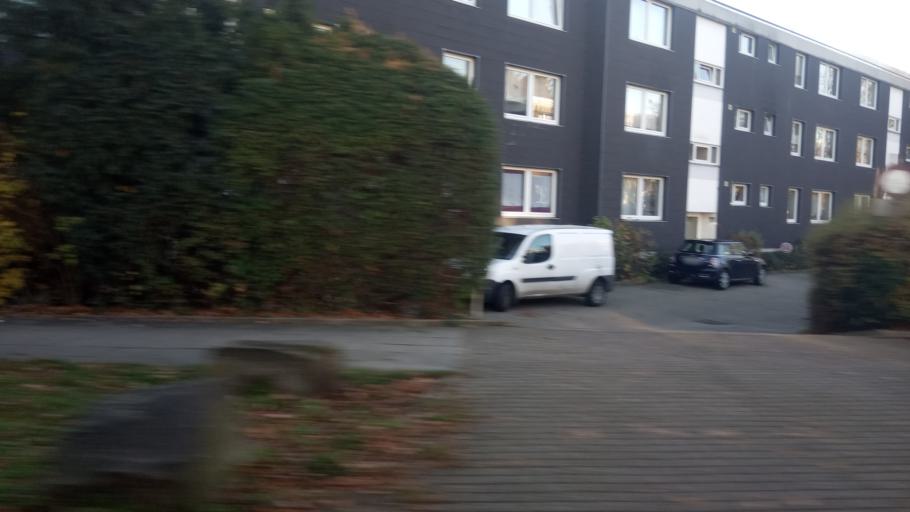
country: DE
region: North Rhine-Westphalia
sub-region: Regierungsbezirk Dusseldorf
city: Velbert
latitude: 51.3874
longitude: 7.0266
